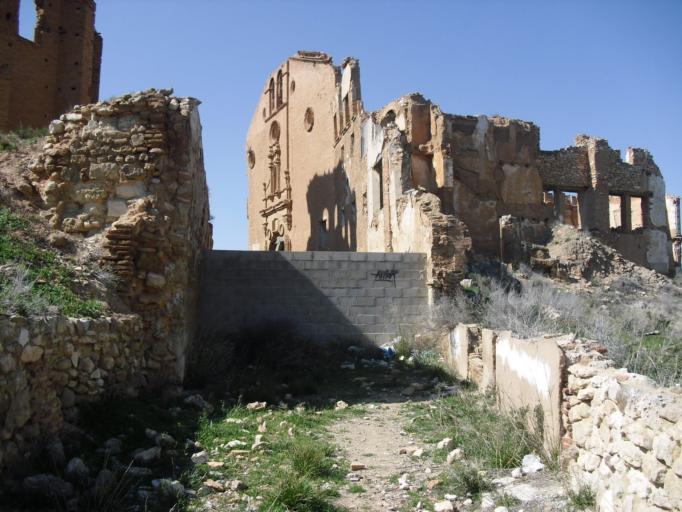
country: ES
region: Aragon
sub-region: Provincia de Zaragoza
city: Belchite
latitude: 41.2994
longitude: -0.7452
